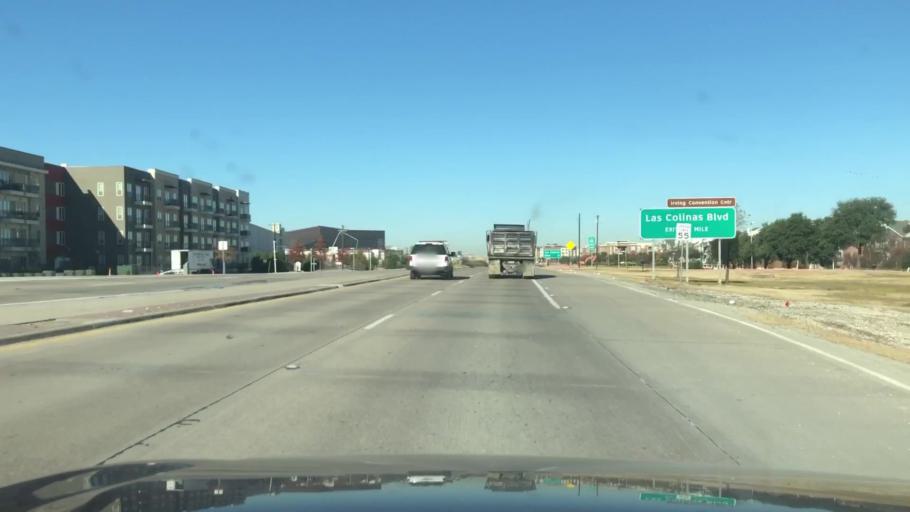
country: US
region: Texas
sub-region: Dallas County
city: Irving
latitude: 32.8747
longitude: -96.9335
